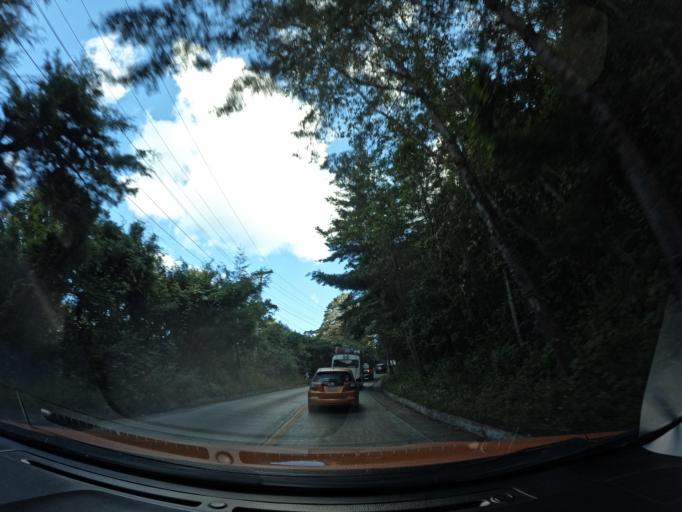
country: GT
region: Sacatepequez
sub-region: Municipio de Santa Maria de Jesus
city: Santa Maria de Jesus
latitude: 14.5105
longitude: -90.7207
